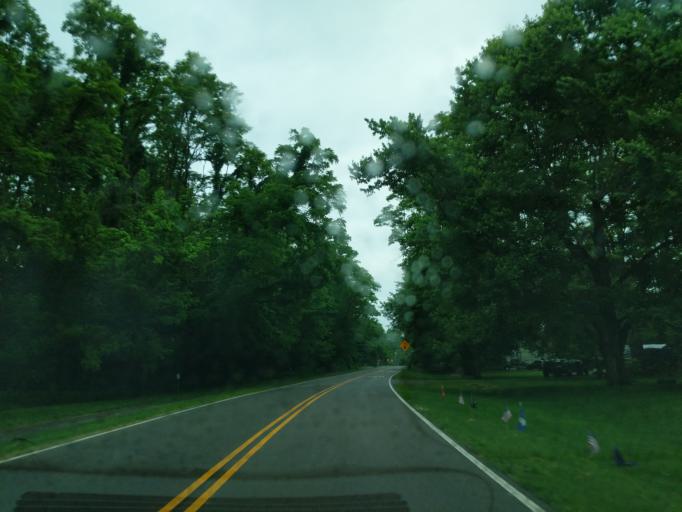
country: US
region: Indiana
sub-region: Madison County
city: Chesterfield
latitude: 40.0986
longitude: -85.6163
